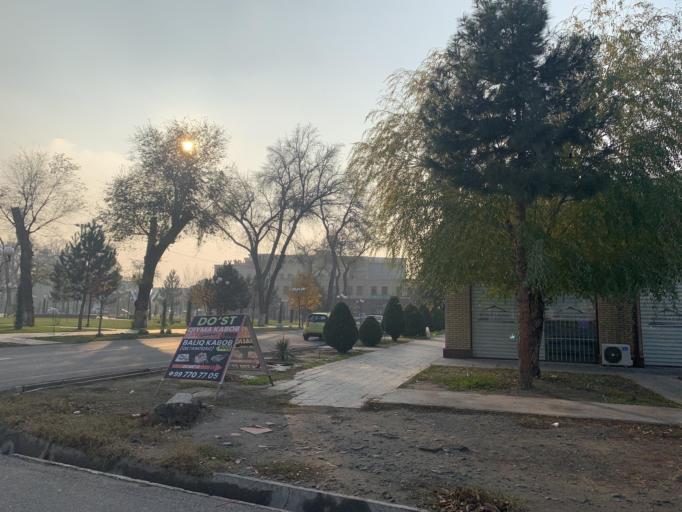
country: UZ
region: Fergana
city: Qo`qon
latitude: 40.5379
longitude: 70.9355
